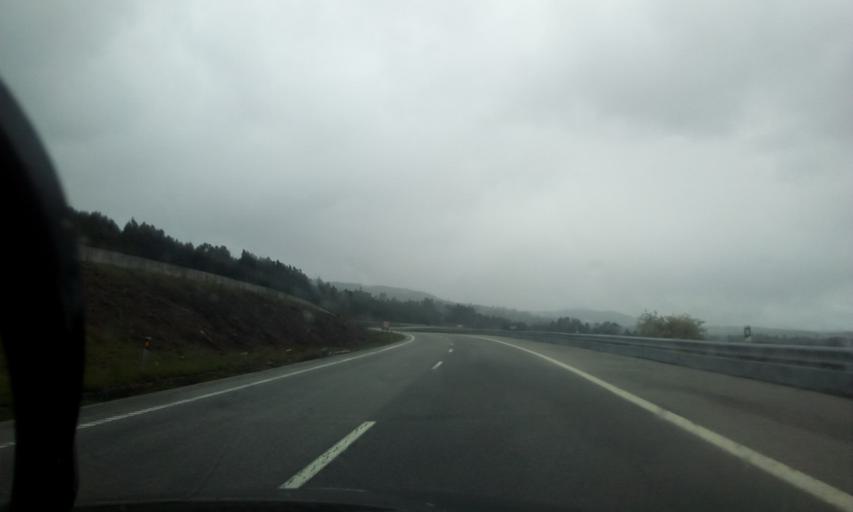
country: PT
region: Viseu
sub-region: Mangualde
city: Mangualde
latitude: 40.6147
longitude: -7.6618
